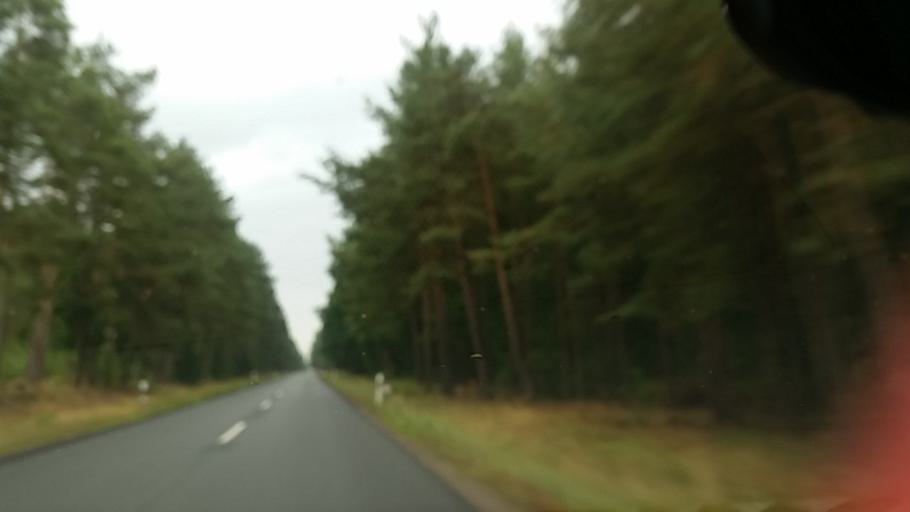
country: DE
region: Lower Saxony
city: Schoneworde
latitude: 52.5818
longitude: 10.6794
